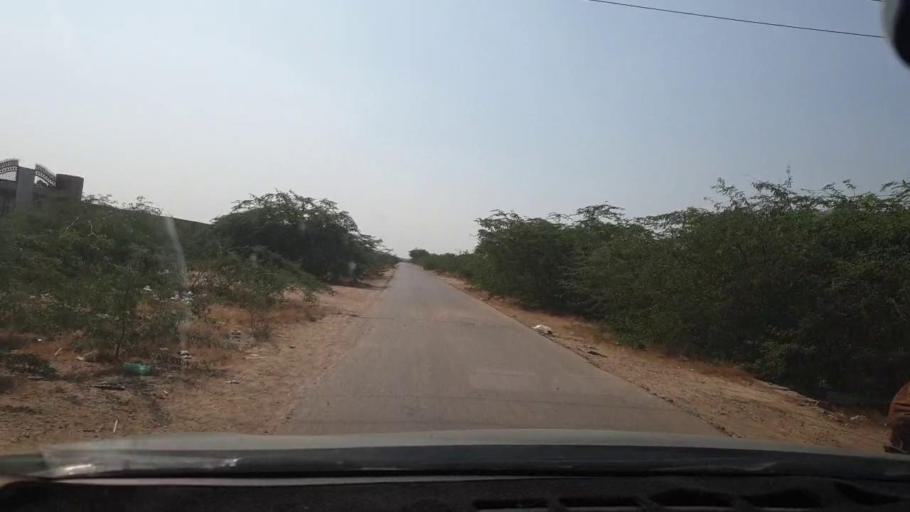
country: PK
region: Sindh
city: Malir Cantonment
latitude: 25.1278
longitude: 67.2256
